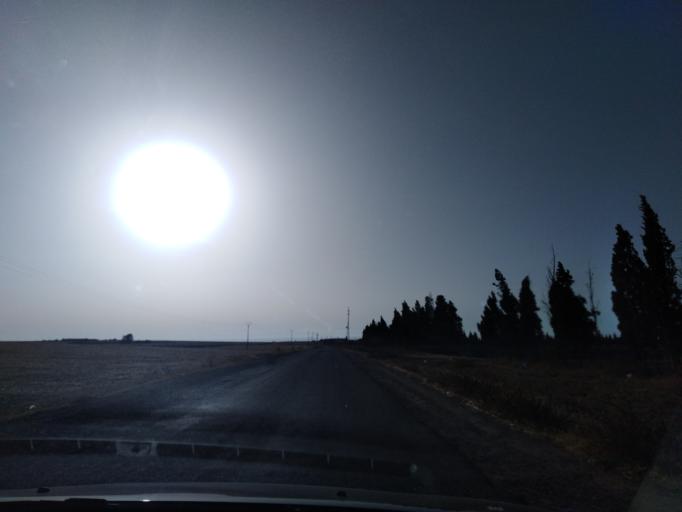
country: MA
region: Doukkala-Abda
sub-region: Safi
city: Safi
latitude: 32.4846
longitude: -8.9143
